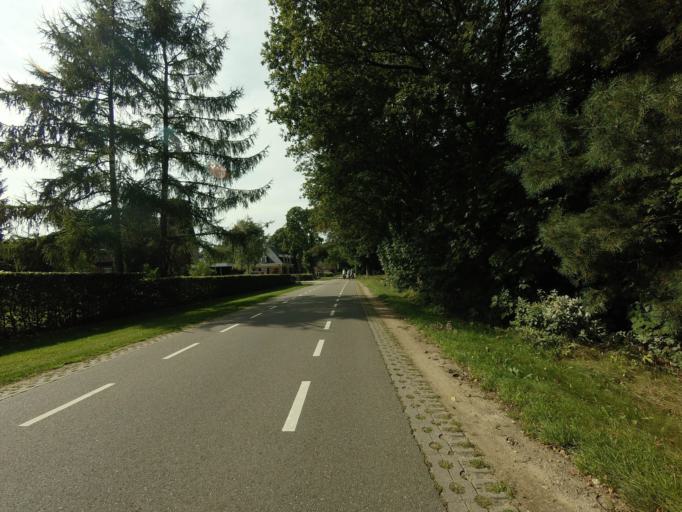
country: NL
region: Overijssel
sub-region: Gemeente Hof van Twente
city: Markelo
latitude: 52.2575
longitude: 6.5368
